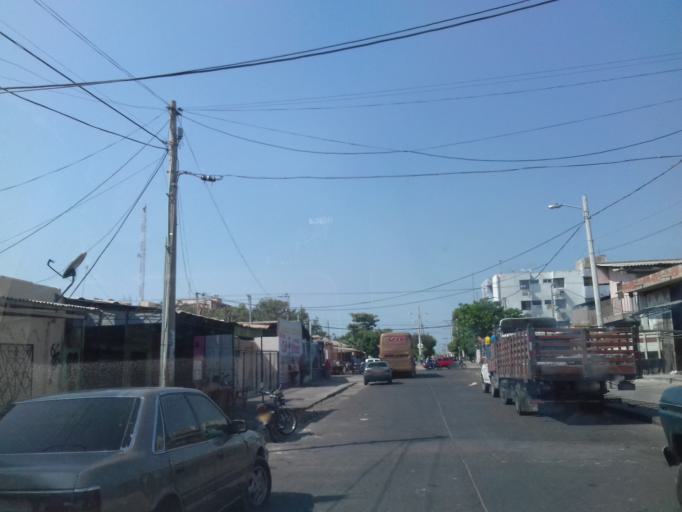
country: CO
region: La Guajira
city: Maicao
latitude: 11.3801
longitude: -72.2388
